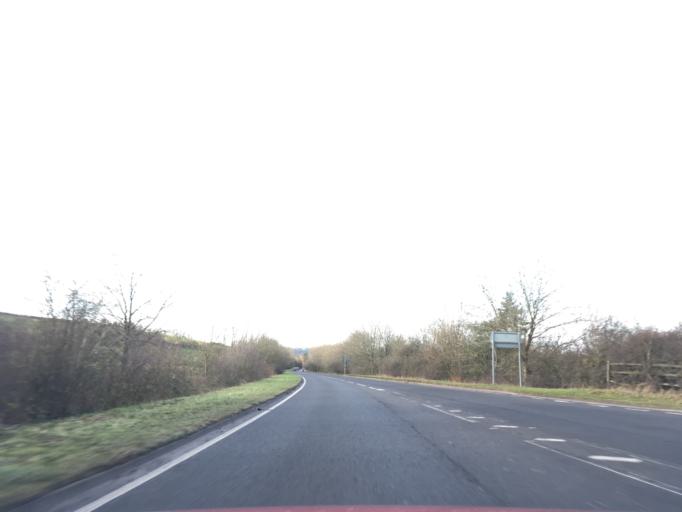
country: GB
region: Wales
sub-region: Monmouthshire
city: Usk
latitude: 51.7053
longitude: -2.8791
